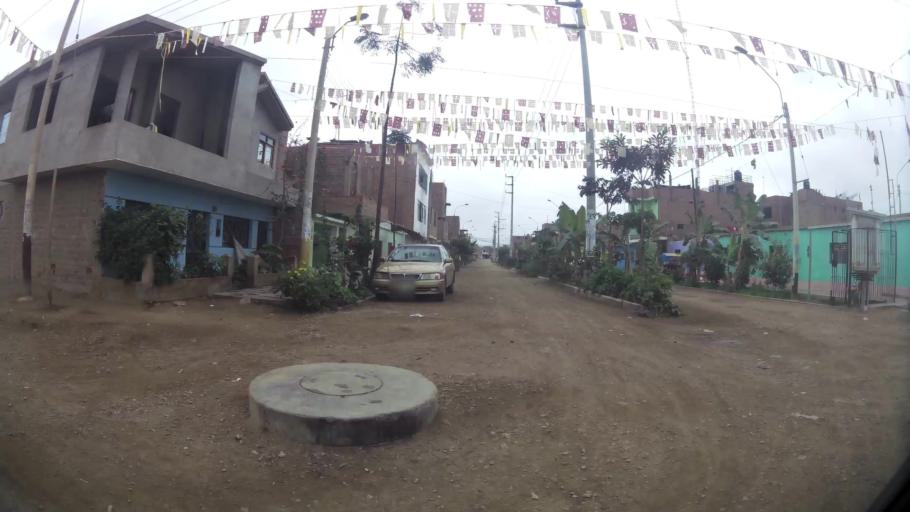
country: PE
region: Lima
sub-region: Provincia de Huaral
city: Huaral
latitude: -11.5035
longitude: -77.2112
